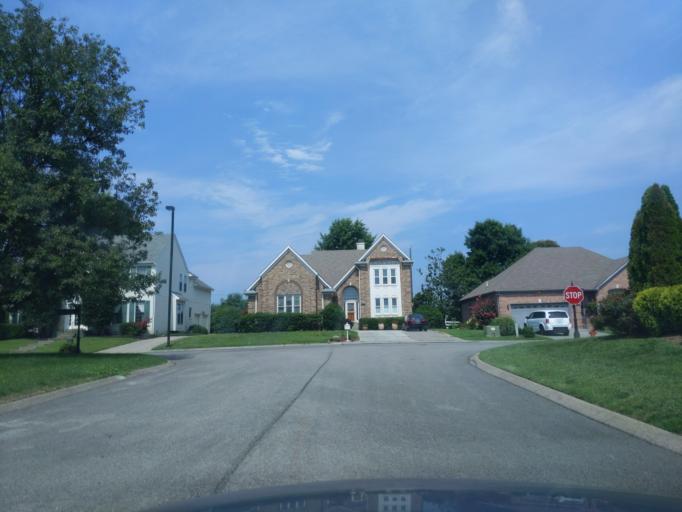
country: US
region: Tennessee
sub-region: Williamson County
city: Brentwood Estates
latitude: 36.0317
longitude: -86.7510
